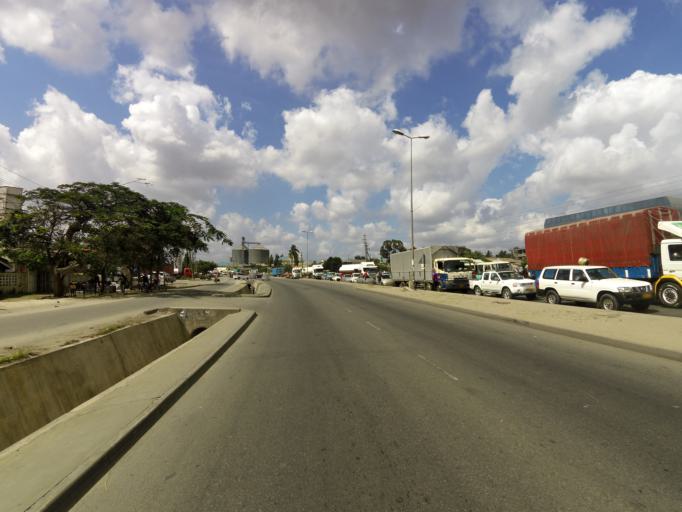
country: TZ
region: Dar es Salaam
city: Magomeni
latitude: -6.7988
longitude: 39.2066
